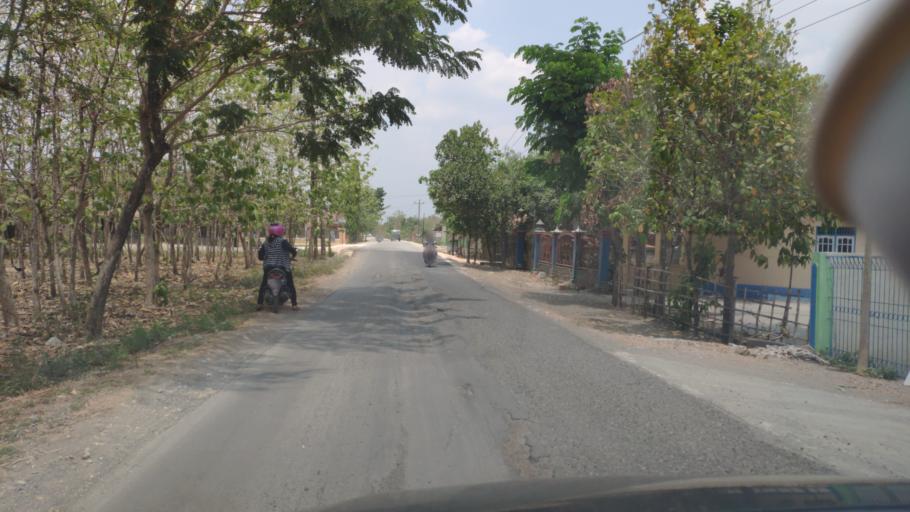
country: ID
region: Central Java
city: Ngablak
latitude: -7.0174
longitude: 111.3813
